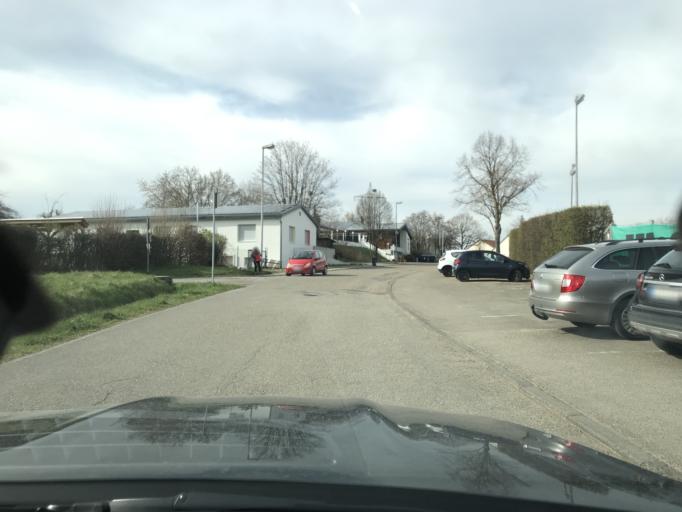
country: DE
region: Baden-Wuerttemberg
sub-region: Regierungsbezirk Stuttgart
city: Waiblingen
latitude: 48.7995
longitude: 9.3161
